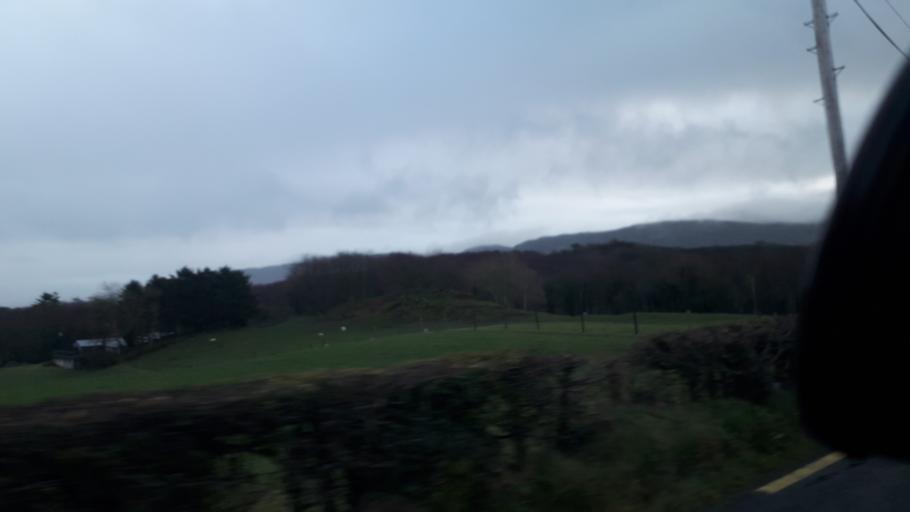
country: IE
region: Ulster
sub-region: County Donegal
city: Ramelton
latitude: 55.1956
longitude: -7.6390
